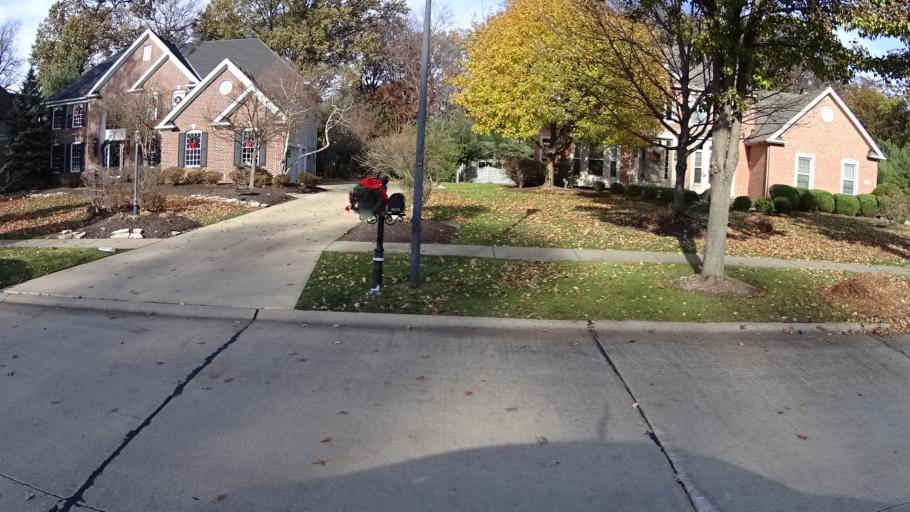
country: US
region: Ohio
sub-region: Cuyahoga County
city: Bay Village
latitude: 41.5007
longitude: -81.9699
